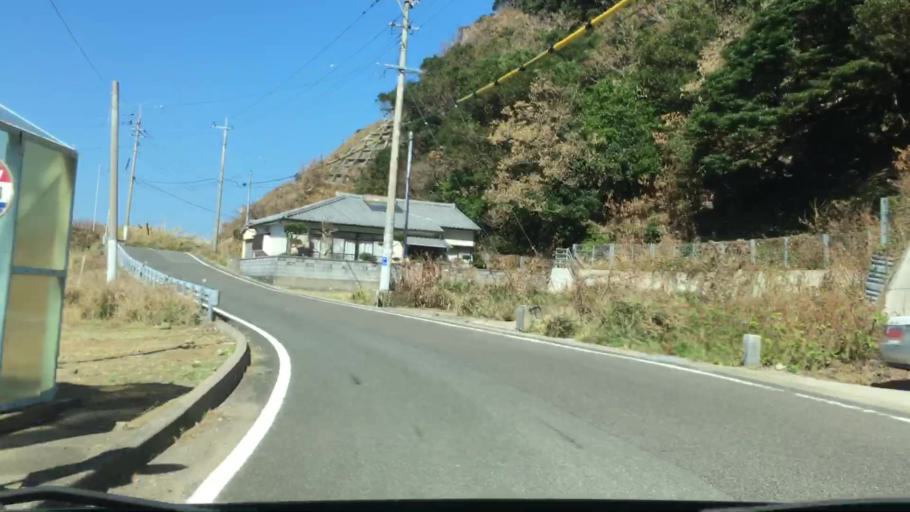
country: JP
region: Nagasaki
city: Sasebo
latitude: 33.0043
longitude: 129.5558
